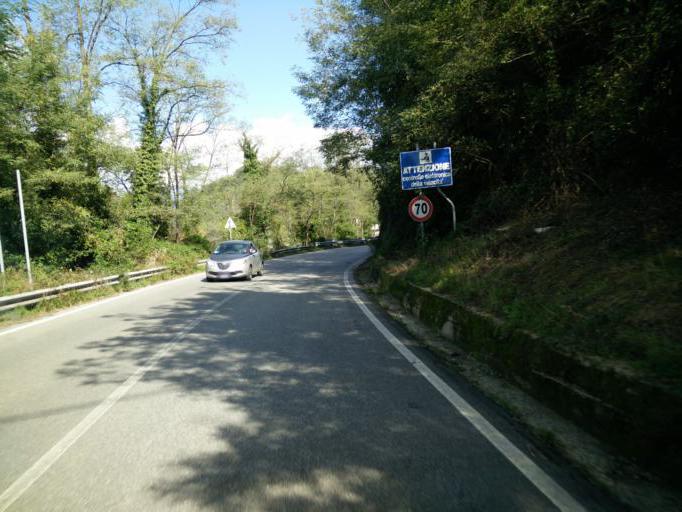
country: IT
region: Liguria
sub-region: Provincia di La Spezia
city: Sesta Godano
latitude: 44.2729
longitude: 9.6574
